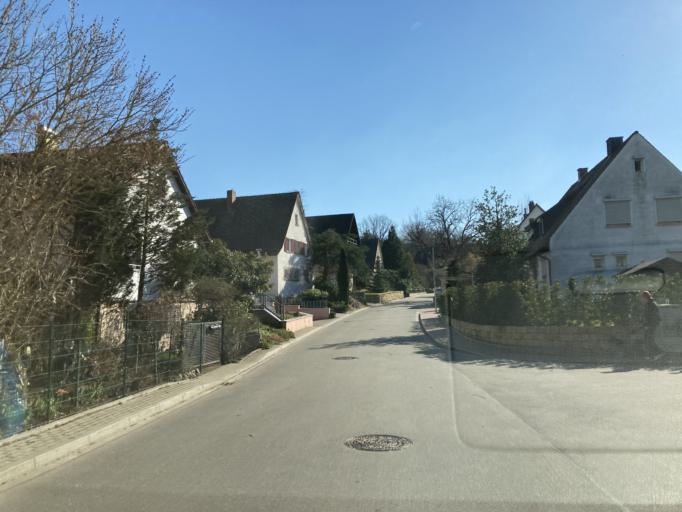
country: DE
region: Baden-Wuerttemberg
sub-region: Freiburg Region
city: Mullheim
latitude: 47.8071
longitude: 7.6374
